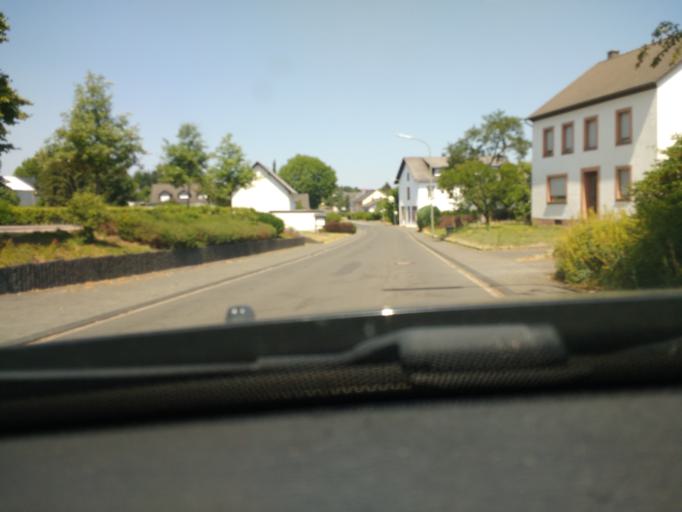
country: DE
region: Rheinland-Pfalz
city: Bettenfeld
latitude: 50.0821
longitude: 6.7591
